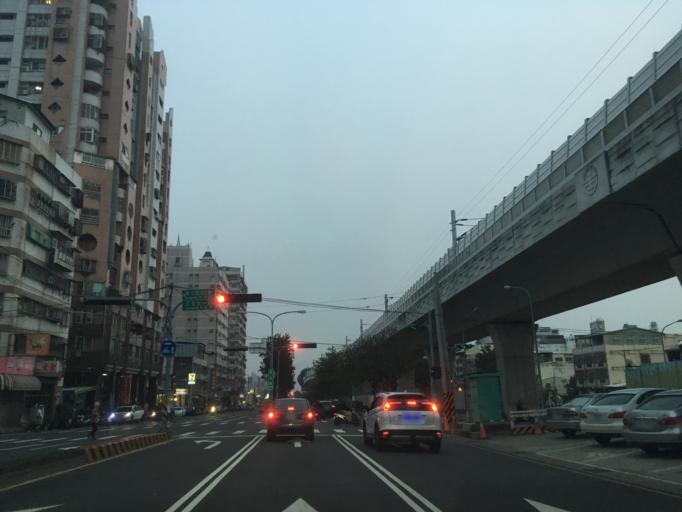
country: TW
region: Taiwan
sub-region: Taichung City
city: Taichung
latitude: 24.1681
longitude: 120.7006
